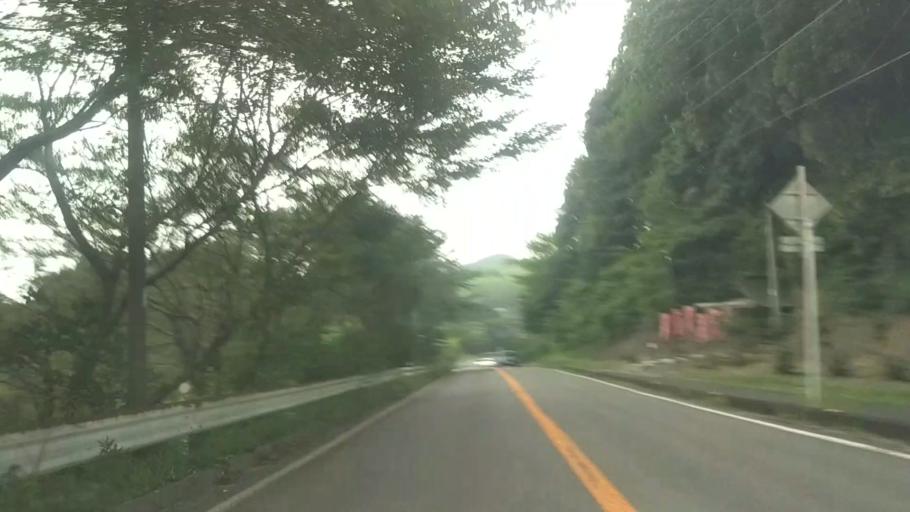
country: JP
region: Chiba
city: Katsuura
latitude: 35.2489
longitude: 140.1952
